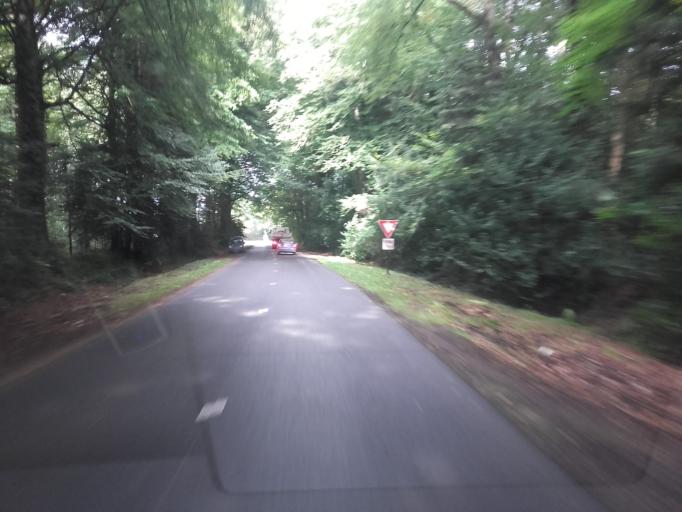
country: FR
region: Brittany
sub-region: Departement des Cotes-d'Armor
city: Plelo
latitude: 48.5895
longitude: -2.9446
